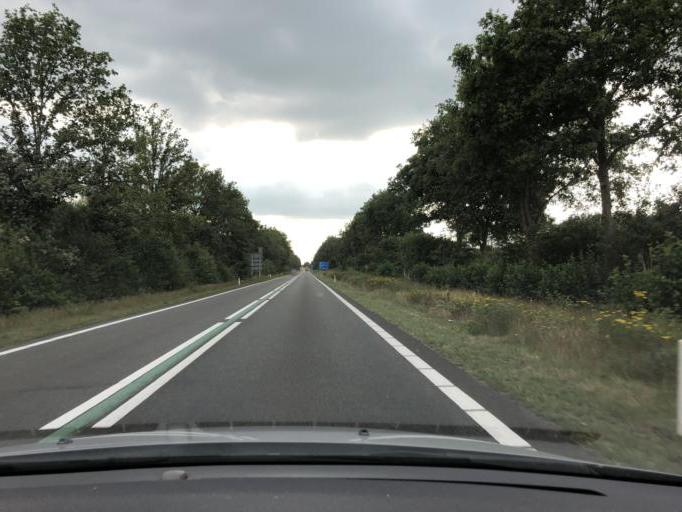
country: NL
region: Drenthe
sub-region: Gemeente Hoogeveen
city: Hoogeveen
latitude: 52.6107
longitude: 6.4764
